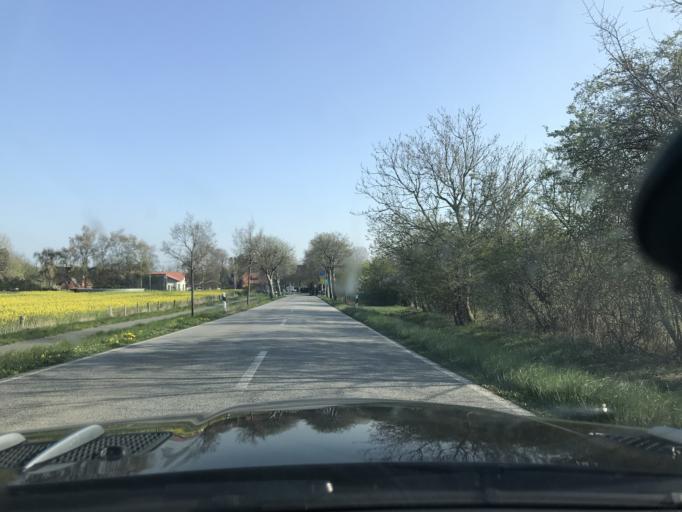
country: DE
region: Schleswig-Holstein
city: Neukirchen
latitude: 54.3620
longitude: 11.0336
